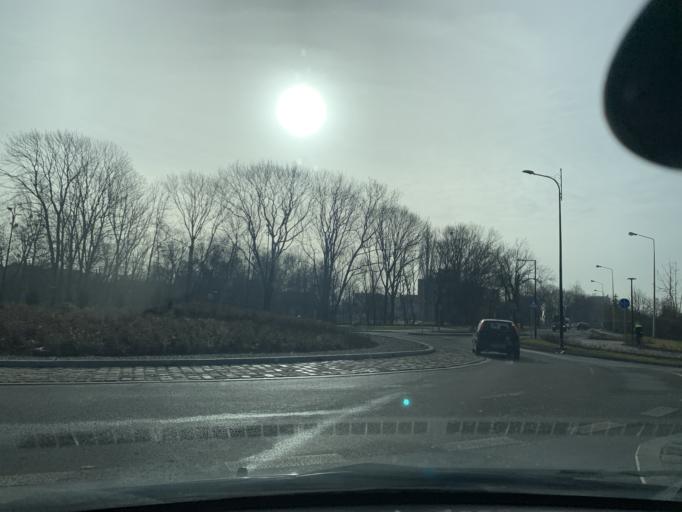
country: PL
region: Silesian Voivodeship
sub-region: Ruda Slaska
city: Ruda Slaska
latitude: 50.3069
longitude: 18.8540
